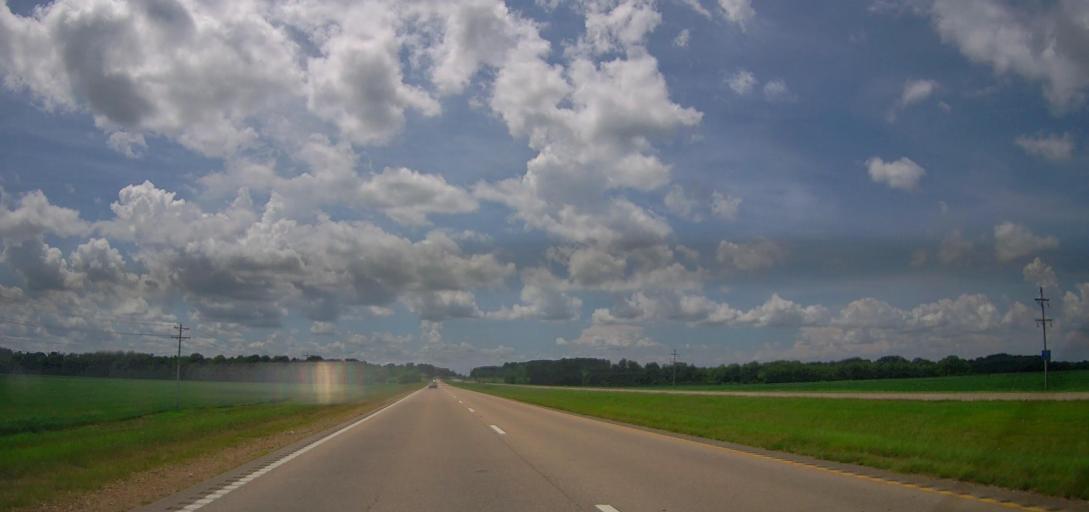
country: US
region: Mississippi
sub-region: Lee County
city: Nettleton
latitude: 34.1016
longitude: -88.6585
